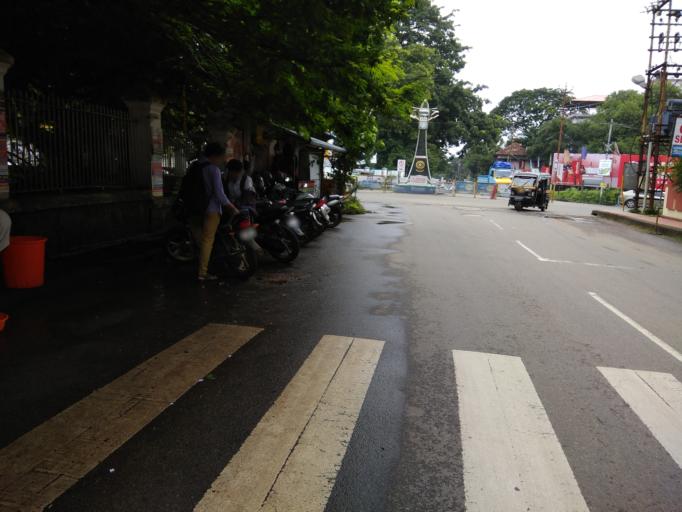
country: IN
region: Kerala
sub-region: Thrissur District
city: Trichur
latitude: 10.5305
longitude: 76.2194
